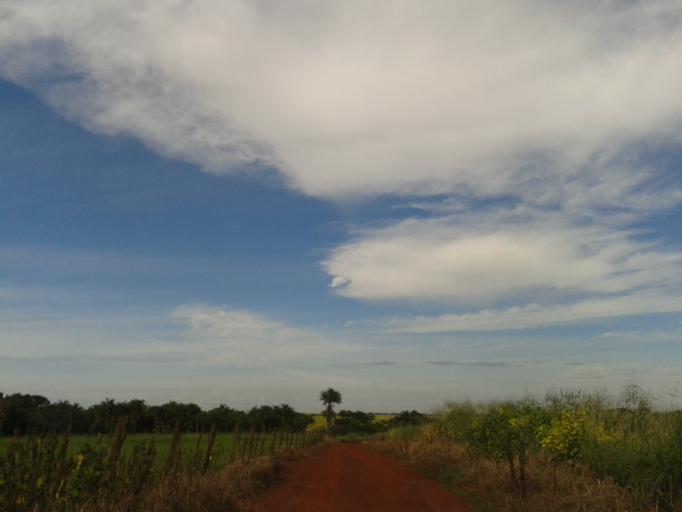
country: BR
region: Minas Gerais
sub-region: Capinopolis
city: Capinopolis
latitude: -18.6532
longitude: -49.6952
